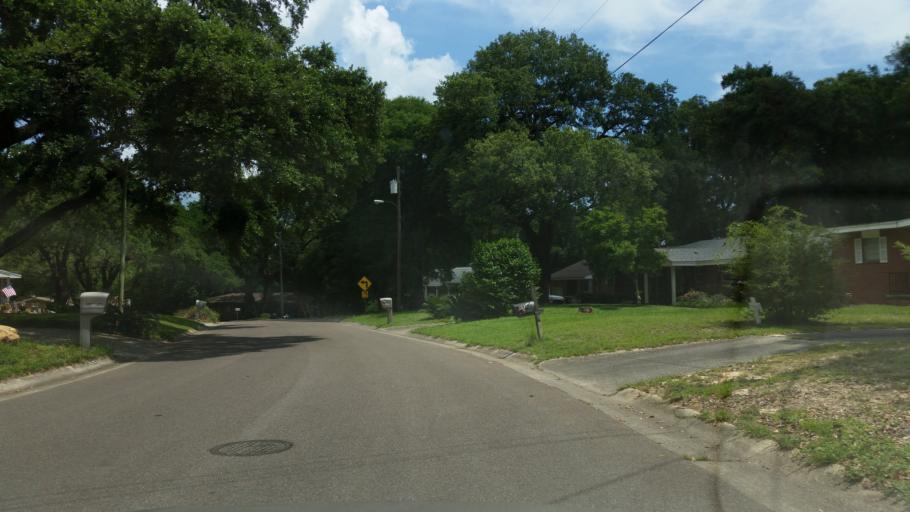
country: US
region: Florida
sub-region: Escambia County
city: Brent
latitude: 30.4826
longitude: -87.2240
